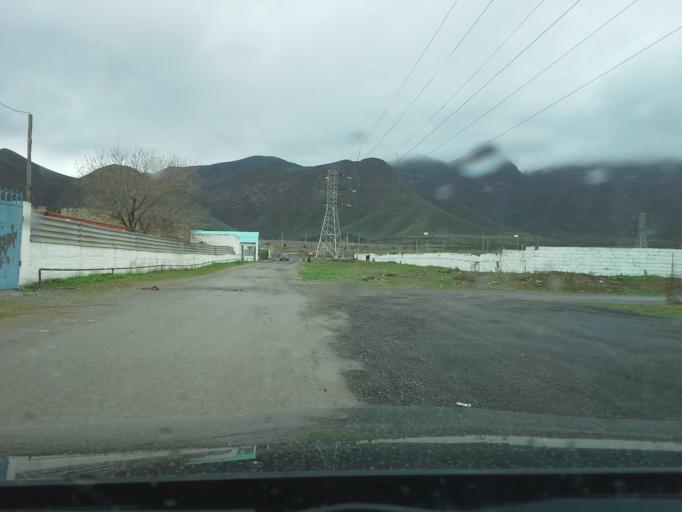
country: TM
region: Ahal
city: Abadan
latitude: 37.9503
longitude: 58.2054
